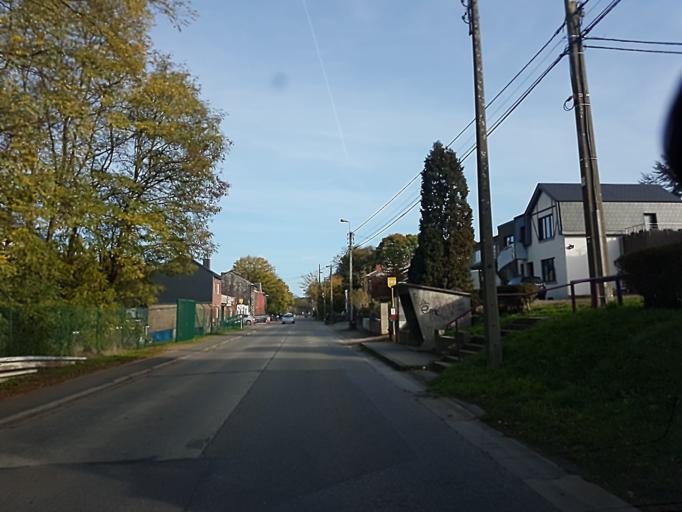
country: BE
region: Wallonia
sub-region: Province de Liege
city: Flemalle-Haute
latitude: 50.5839
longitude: 5.4348
